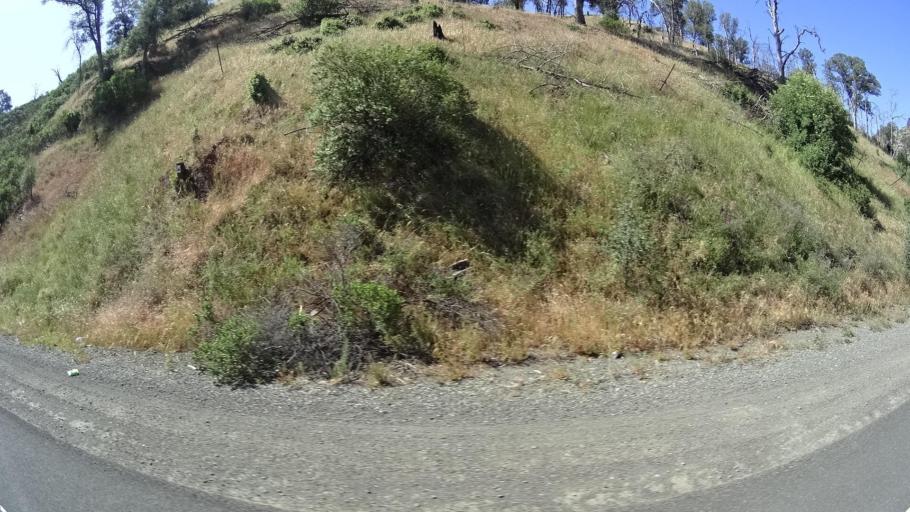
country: US
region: California
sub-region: Lake County
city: Clearlake
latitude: 39.0177
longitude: -122.5826
